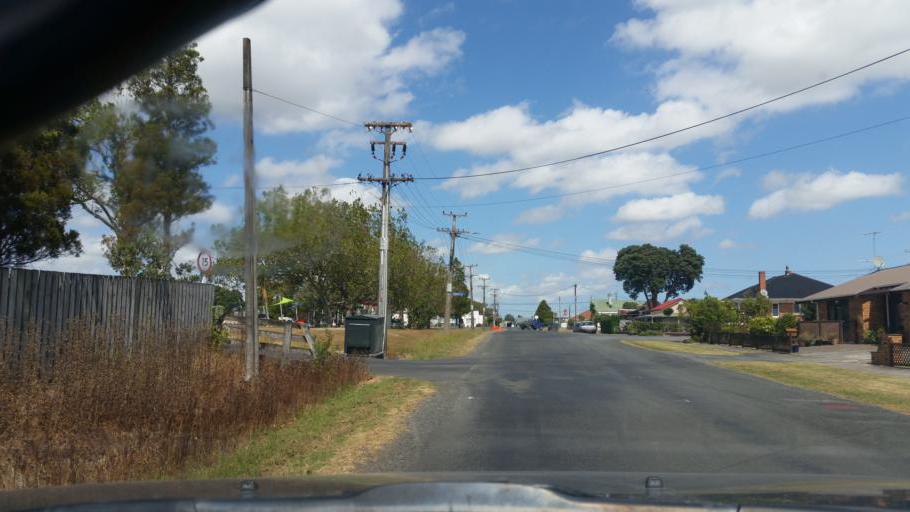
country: NZ
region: Northland
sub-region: Kaipara District
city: Dargaville
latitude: -35.9345
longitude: 173.8756
